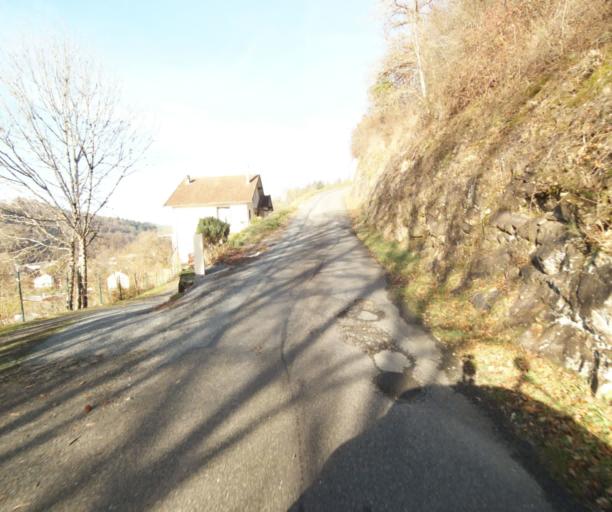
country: FR
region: Limousin
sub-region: Departement de la Correze
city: Laguenne
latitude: 45.2434
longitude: 1.7801
